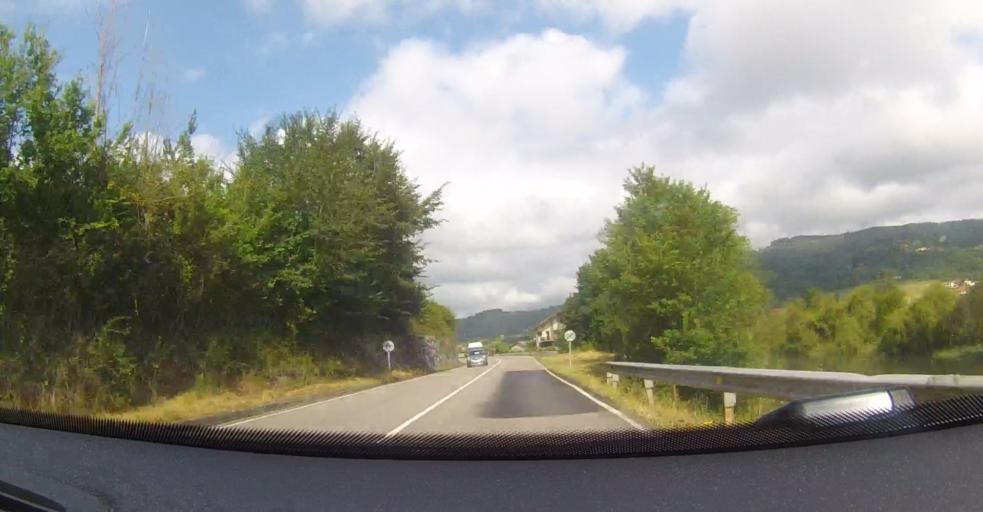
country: ES
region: Asturias
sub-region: Province of Asturias
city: Villaviciosa
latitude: 43.4889
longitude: -5.4392
